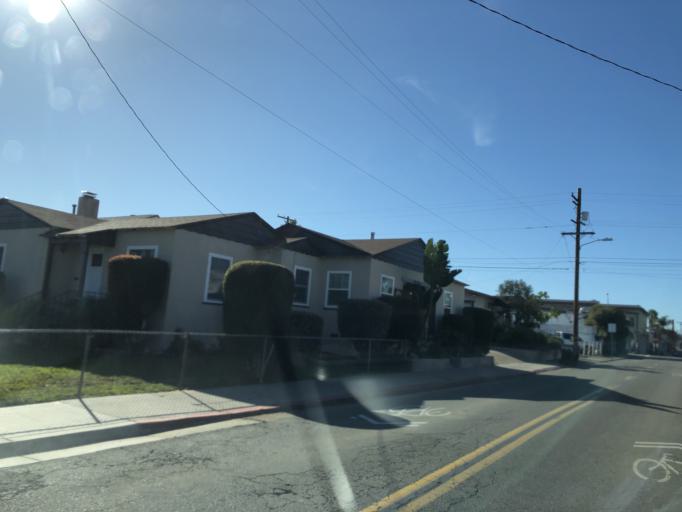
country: US
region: California
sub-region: San Diego County
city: San Diego
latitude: 32.7411
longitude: -117.1283
